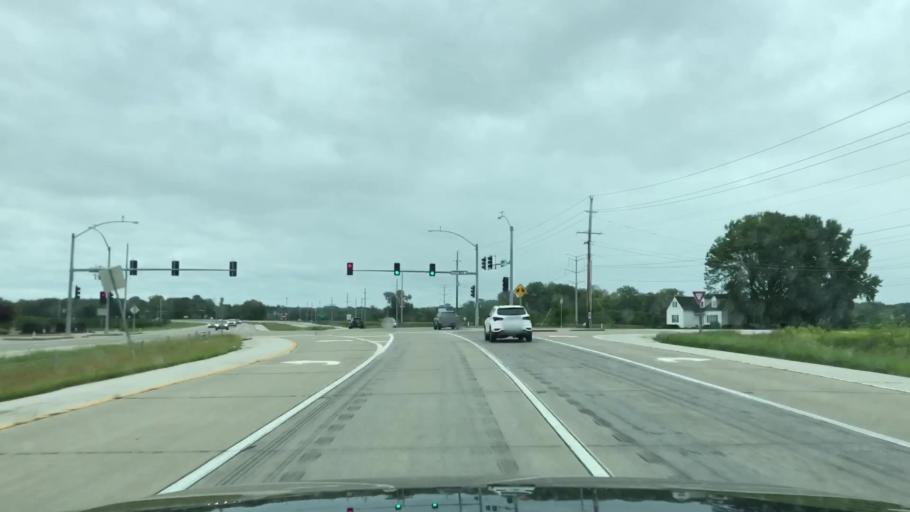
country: US
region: Missouri
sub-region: Saint Charles County
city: Saint Charles
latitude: 38.7297
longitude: -90.4879
